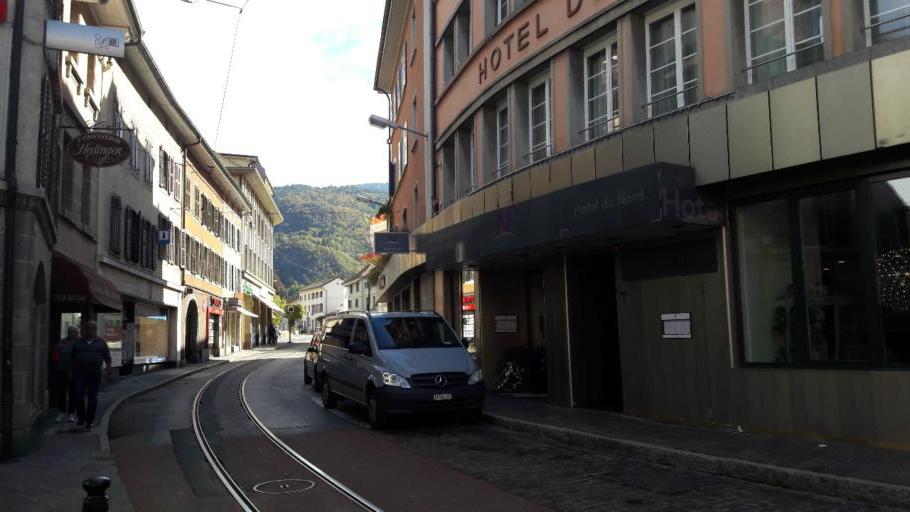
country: CH
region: Vaud
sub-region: Aigle District
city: Aigle
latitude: 46.3181
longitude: 6.9689
